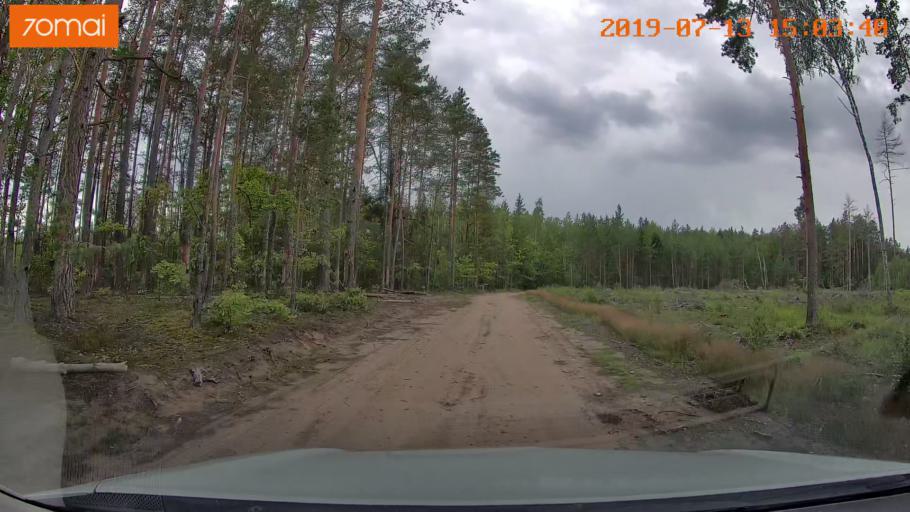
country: BY
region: Mogilev
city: Asipovichy
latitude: 53.2079
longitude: 28.7492
